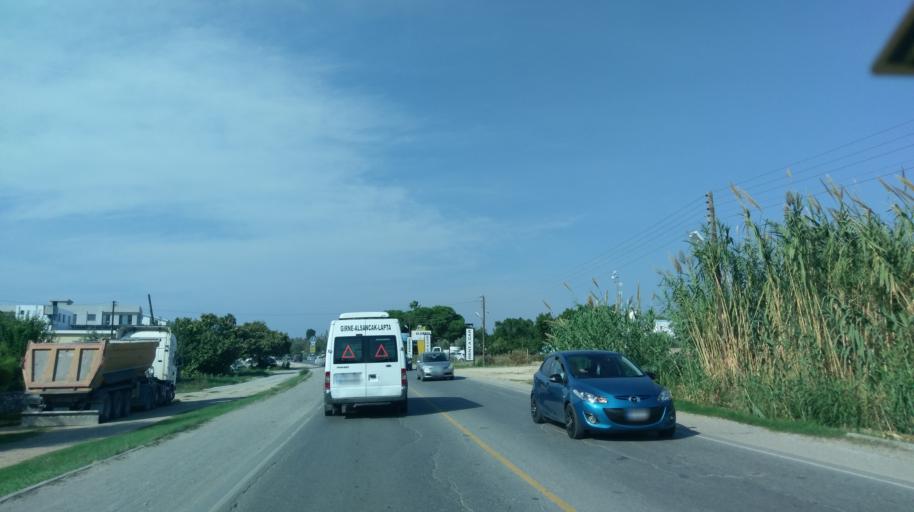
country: CY
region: Keryneia
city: Lapithos
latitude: 35.3475
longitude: 33.2262
